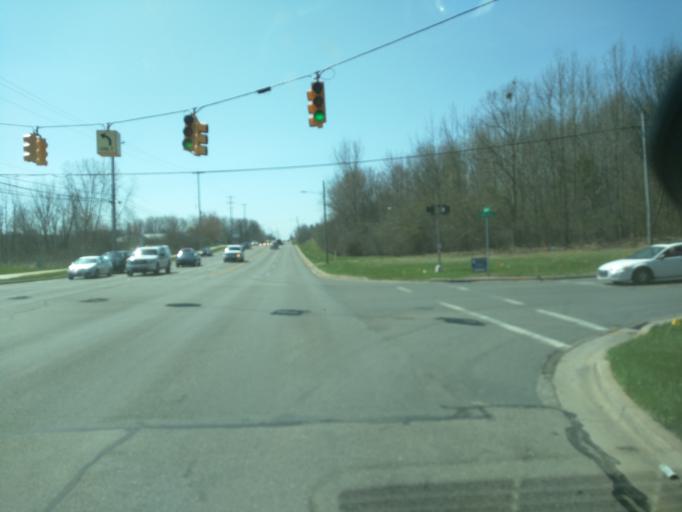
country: US
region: Michigan
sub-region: Kent County
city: East Grand Rapids
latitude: 42.9379
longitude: -85.5704
